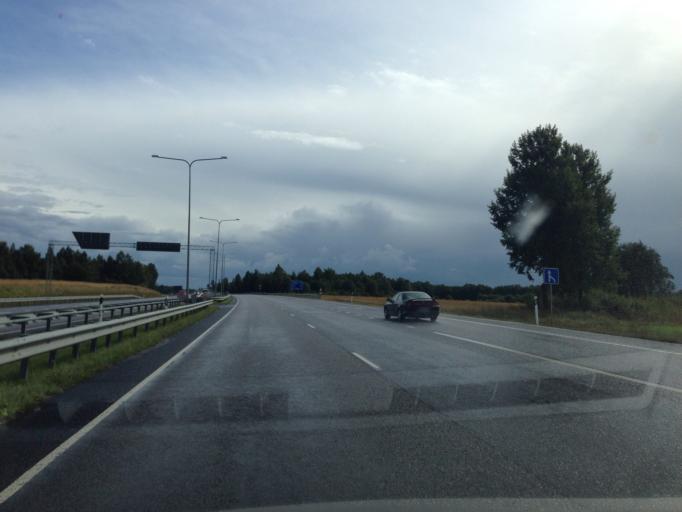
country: EE
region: Jaervamaa
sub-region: Paide linn
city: Paide
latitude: 58.9143
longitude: 25.6221
